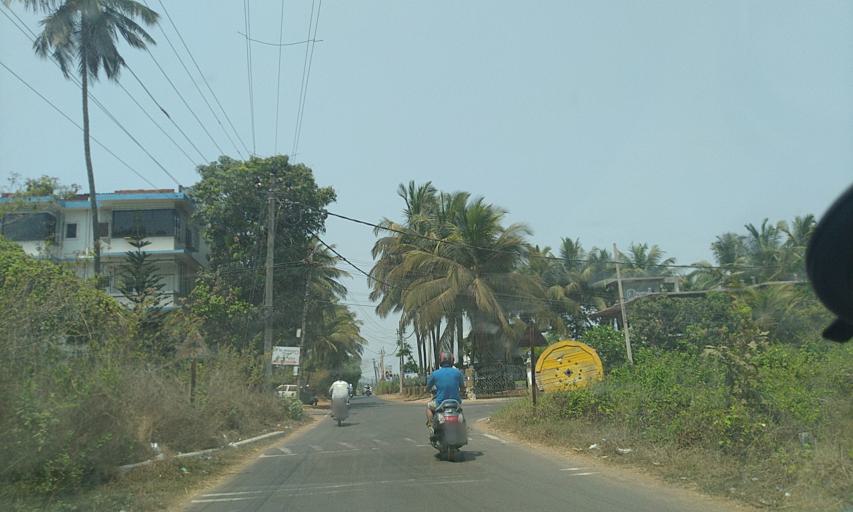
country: IN
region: Goa
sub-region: North Goa
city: Saligao
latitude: 15.5528
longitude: 73.8064
